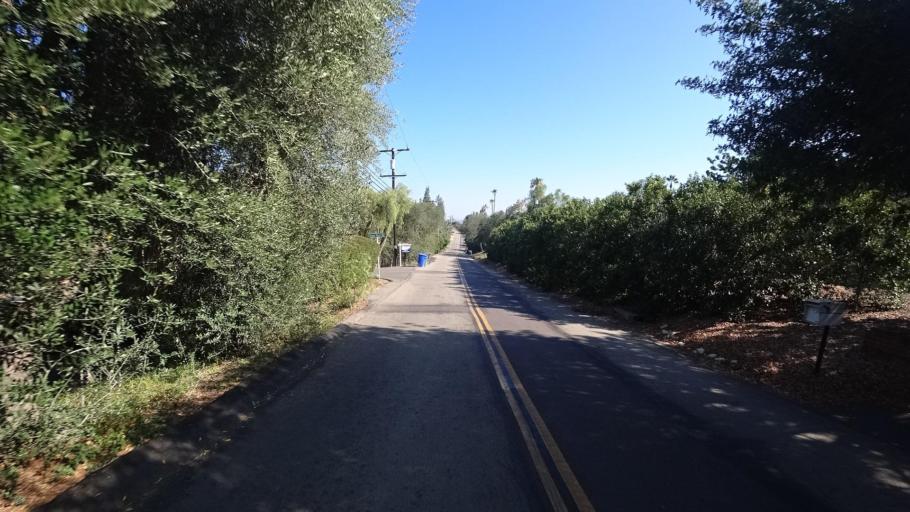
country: US
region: California
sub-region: San Diego County
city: Fallbrook
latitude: 33.3955
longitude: -117.2407
